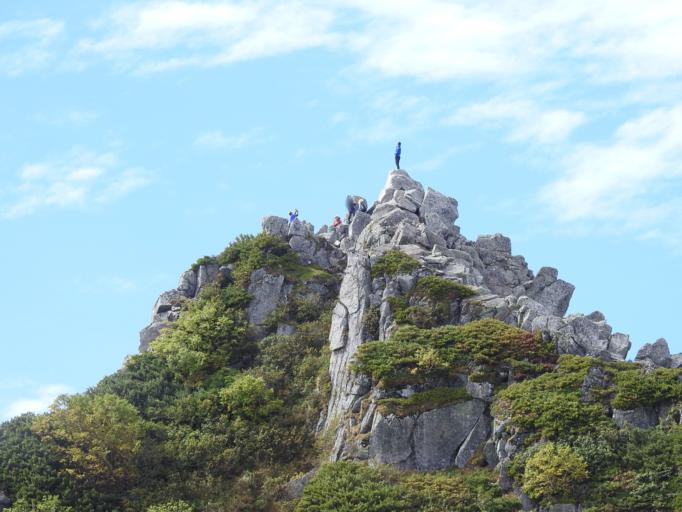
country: JP
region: Nagano
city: Ina
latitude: 35.7833
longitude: 137.8105
